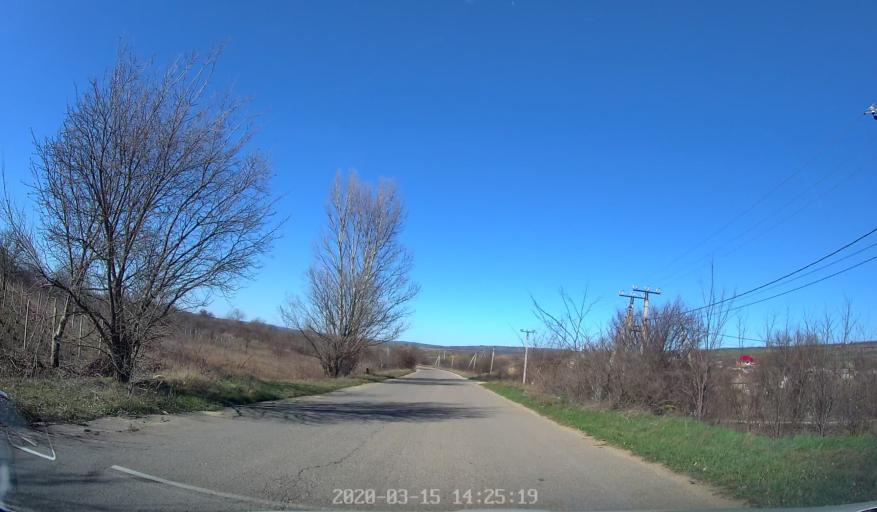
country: MD
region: Orhei
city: Orhei
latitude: 47.3371
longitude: 28.9171
